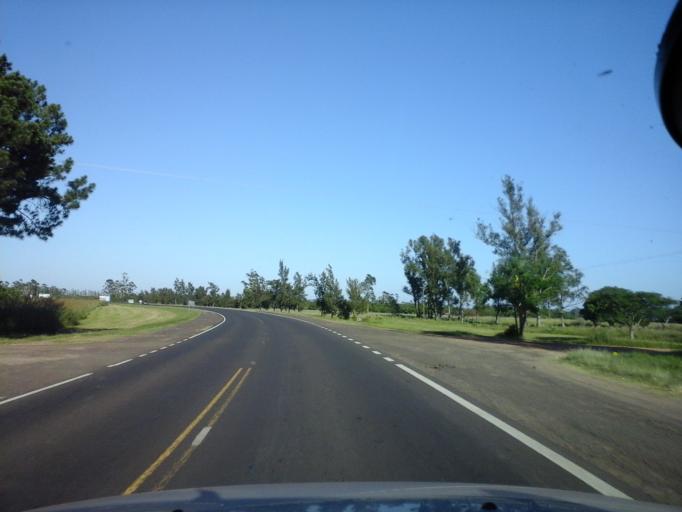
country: AR
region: Corrientes
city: Ita Ibate
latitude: -27.4396
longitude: -57.3442
